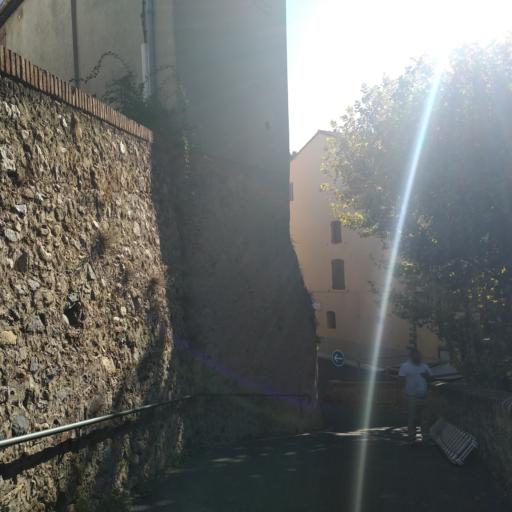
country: FR
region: Languedoc-Roussillon
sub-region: Departement des Pyrenees-Orientales
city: la Roca d'Albera
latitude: 42.5204
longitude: 2.9331
